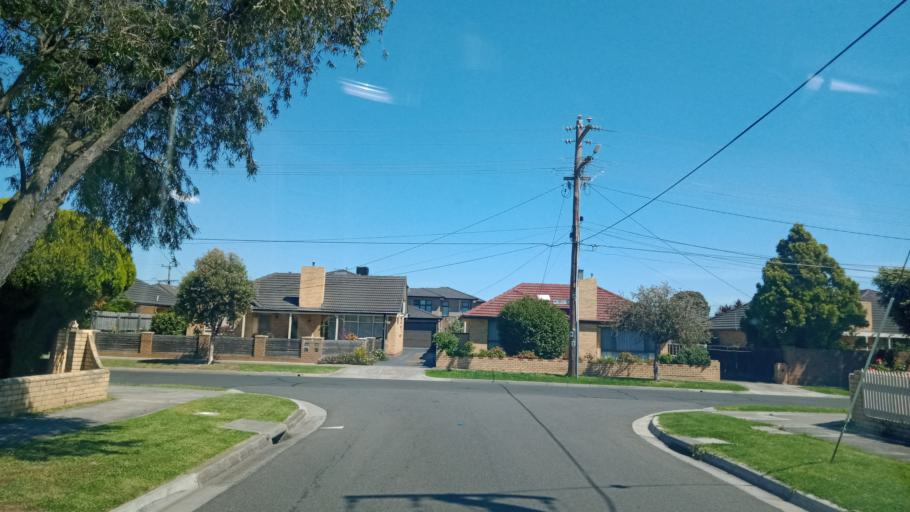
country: AU
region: Victoria
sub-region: Greater Dandenong
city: Springvale
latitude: -37.9322
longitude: 145.1626
